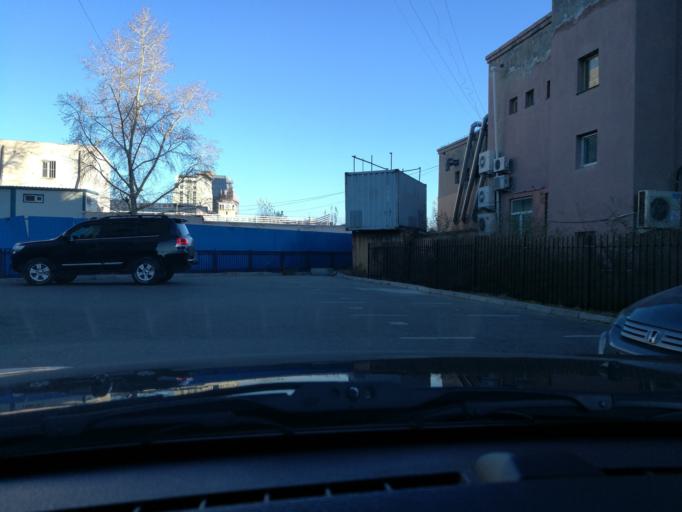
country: MN
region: Ulaanbaatar
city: Ulaanbaatar
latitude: 47.9148
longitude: 106.9170
